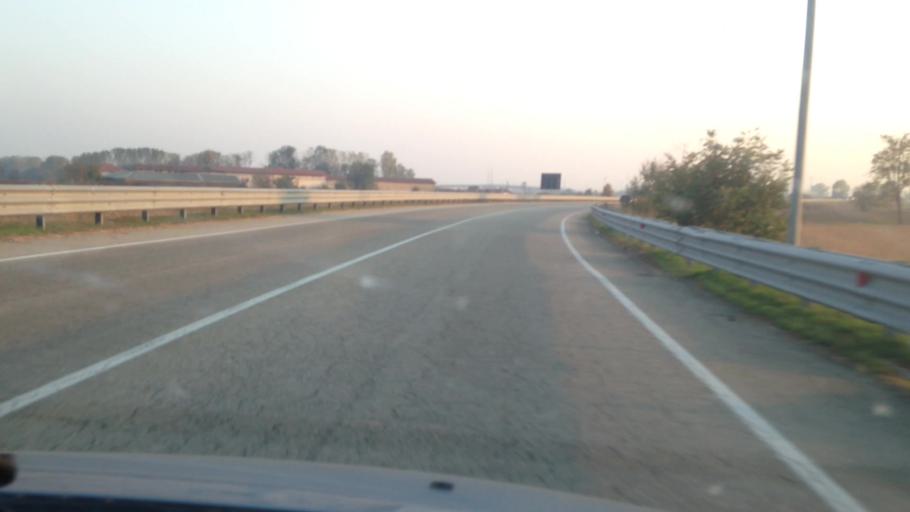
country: IT
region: Piedmont
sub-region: Provincia di Vercelli
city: Cigliano
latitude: 45.3111
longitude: 8.0416
